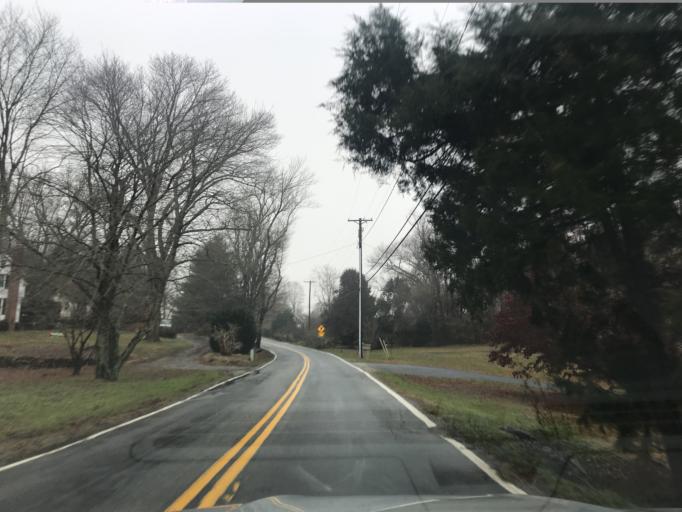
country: US
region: Maryland
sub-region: Harford County
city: South Bel Air
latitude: 39.5757
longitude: -76.2906
